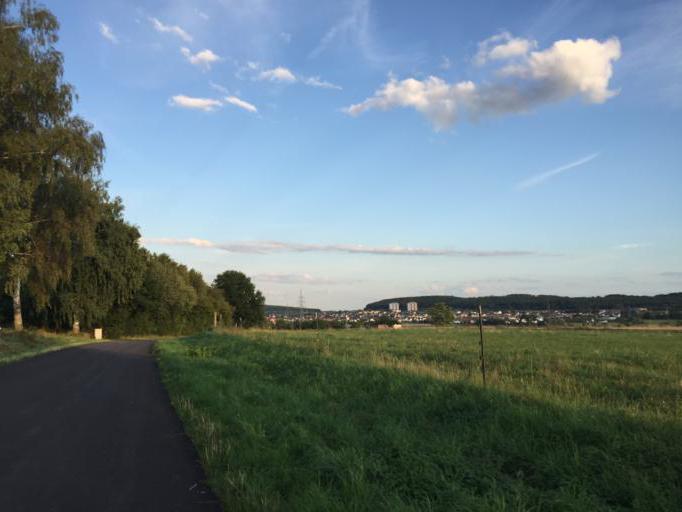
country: DE
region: Hesse
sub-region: Regierungsbezirk Giessen
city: Alten Buseck
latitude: 50.6187
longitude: 8.7644
